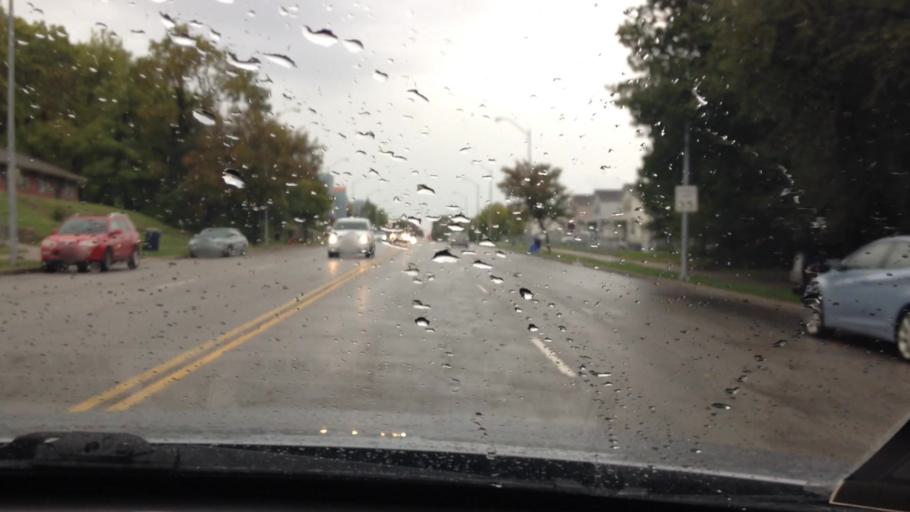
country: US
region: Kansas
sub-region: Johnson County
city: Westwood
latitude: 39.0490
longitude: -94.5678
